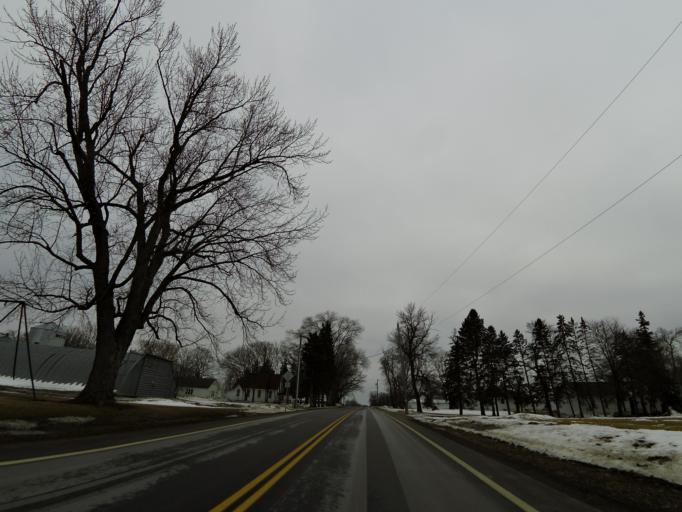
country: US
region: Minnesota
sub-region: Washington County
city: Afton
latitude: 44.8283
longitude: -92.7992
